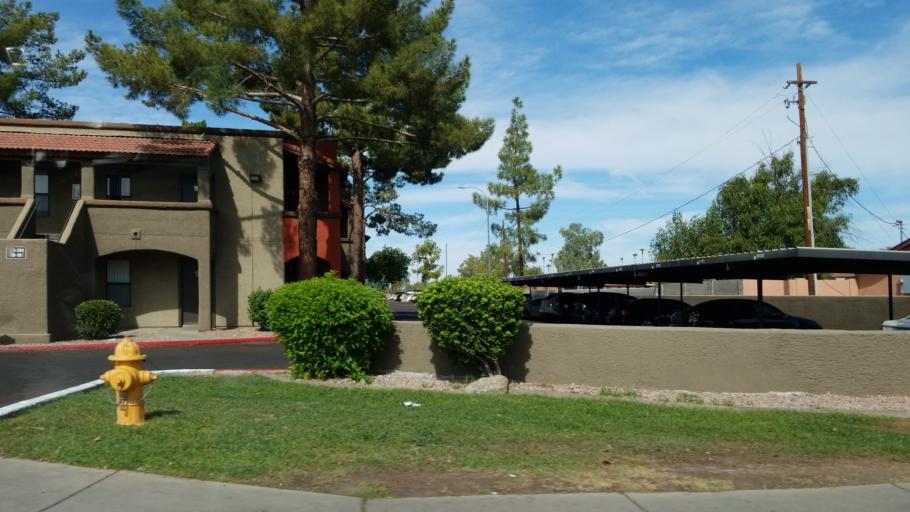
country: US
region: Arizona
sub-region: Maricopa County
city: Glendale
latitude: 33.5221
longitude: -112.1864
